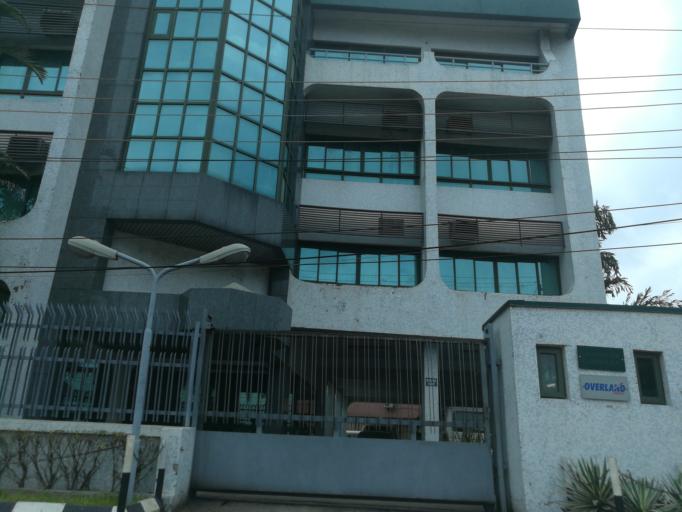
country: NG
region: Lagos
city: Ikeja
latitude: 6.5931
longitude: 3.3388
